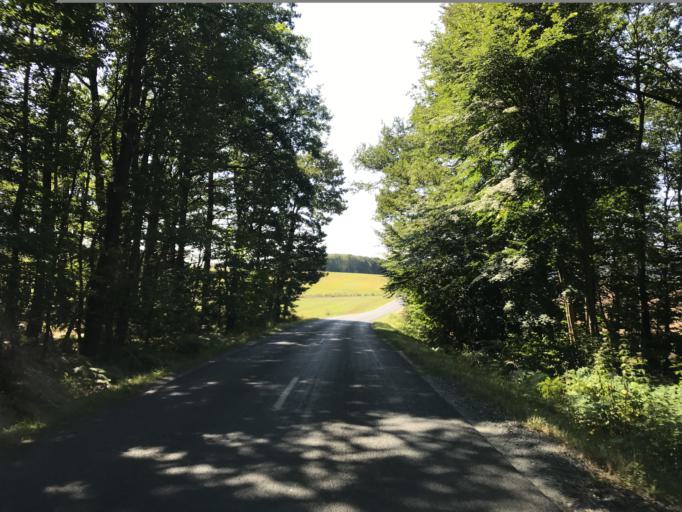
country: FR
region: Haute-Normandie
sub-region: Departement de l'Eure
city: Houlbec-Cocherel
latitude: 49.0840
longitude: 1.3226
